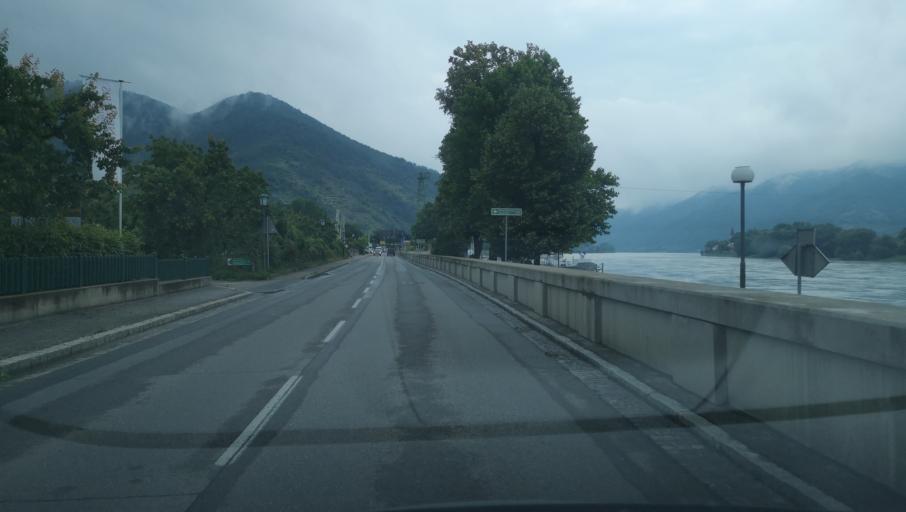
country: AT
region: Lower Austria
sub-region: Politischer Bezirk Krems
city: Spitz
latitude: 48.3605
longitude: 15.4147
